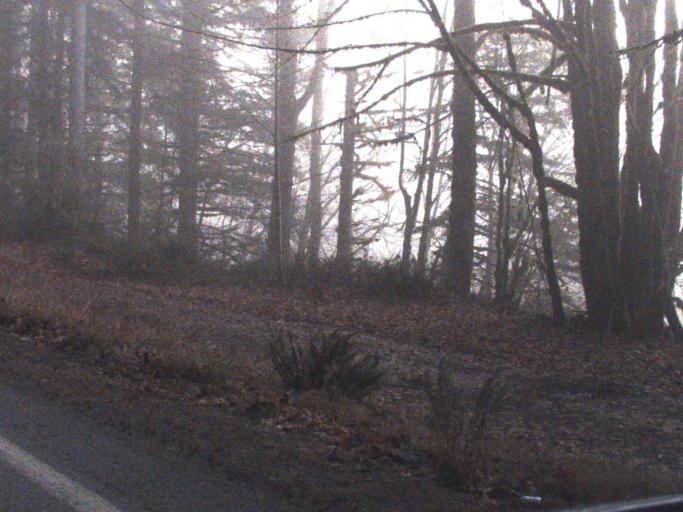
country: US
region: Washington
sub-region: Snohomish County
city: Darrington
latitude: 48.4921
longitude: -121.5649
